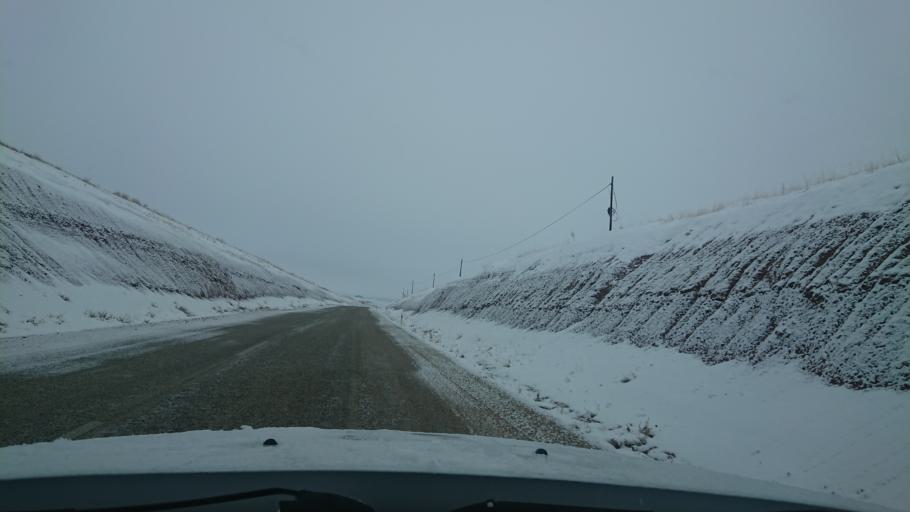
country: TR
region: Aksaray
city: Agacoren
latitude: 38.7738
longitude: 33.8695
